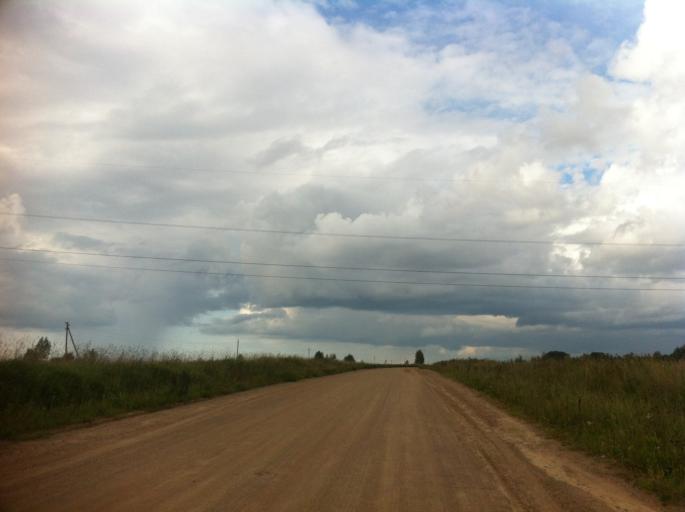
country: RU
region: Pskov
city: Izborsk
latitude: 57.8306
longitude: 27.9829
